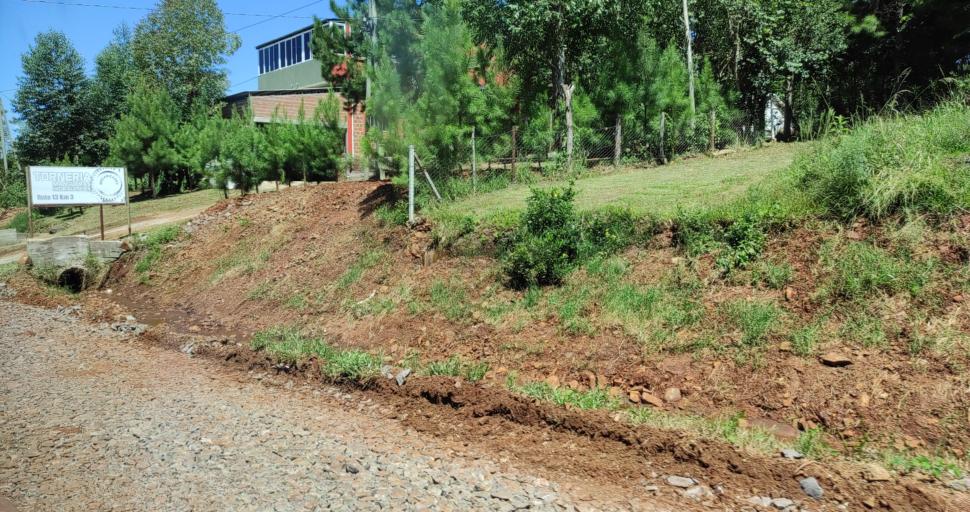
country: AR
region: Misiones
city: El Soberbio
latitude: -27.2880
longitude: -54.2168
